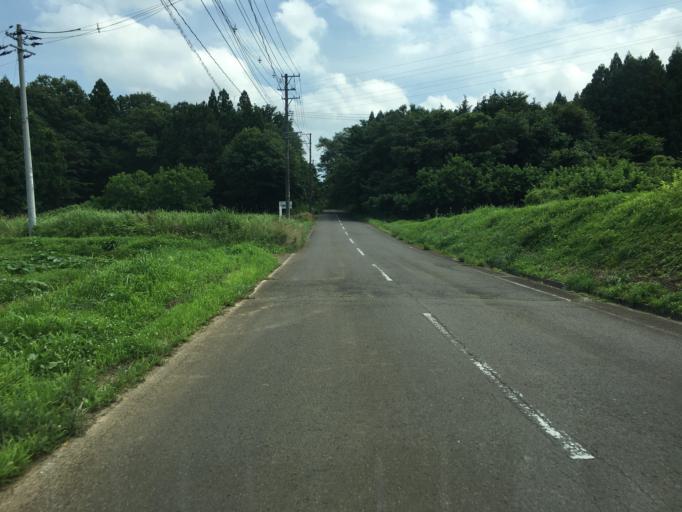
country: JP
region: Fukushima
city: Nihommatsu
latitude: 37.6315
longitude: 140.4549
